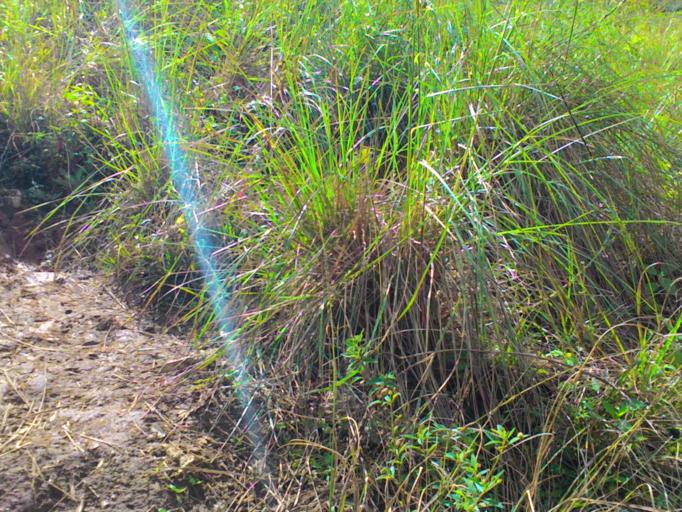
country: HT
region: Sud
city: Les Anglais
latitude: 18.4503
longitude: -74.1051
